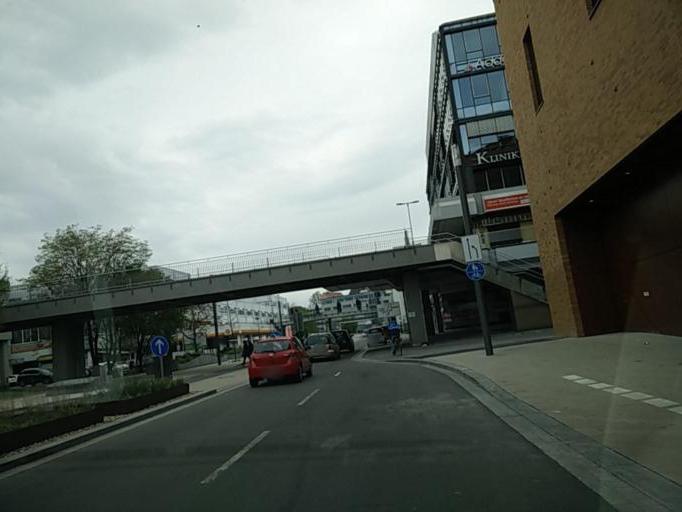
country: DE
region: Baden-Wuerttemberg
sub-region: Regierungsbezirk Stuttgart
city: Boeblingen
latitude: 48.6885
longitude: 9.0074
